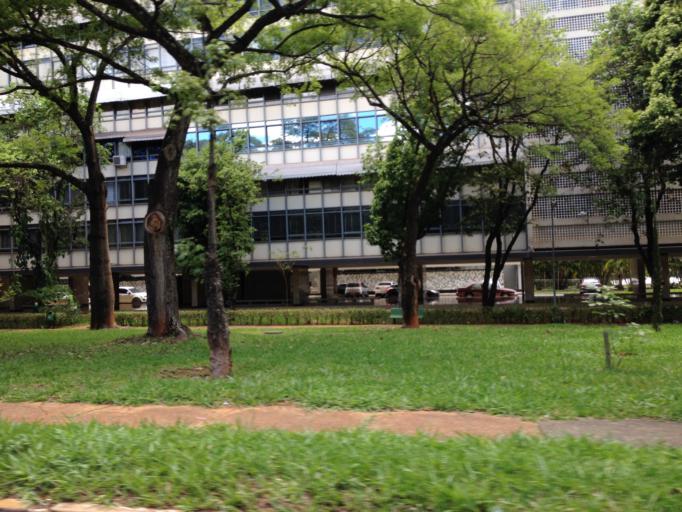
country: BR
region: Federal District
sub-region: Brasilia
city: Brasilia
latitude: -15.8278
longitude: -47.9214
